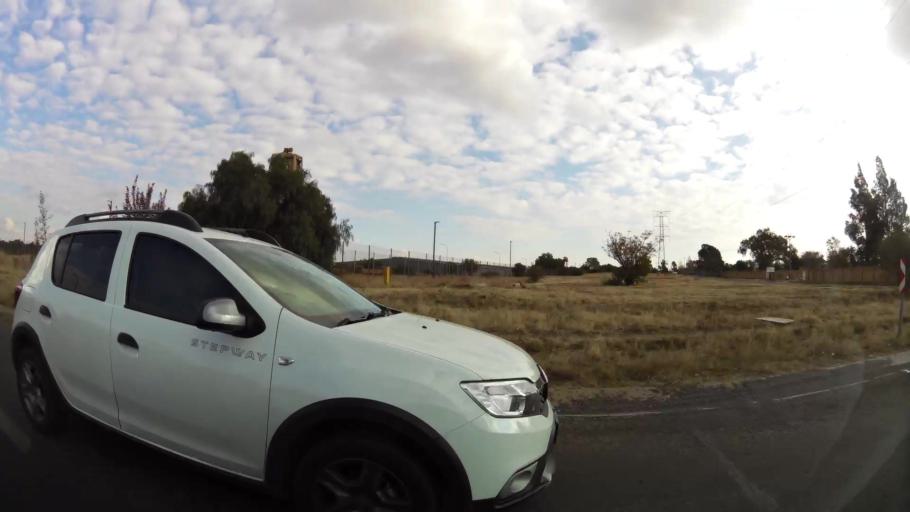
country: ZA
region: Orange Free State
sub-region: Mangaung Metropolitan Municipality
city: Bloemfontein
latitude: -29.0759
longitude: 26.1920
